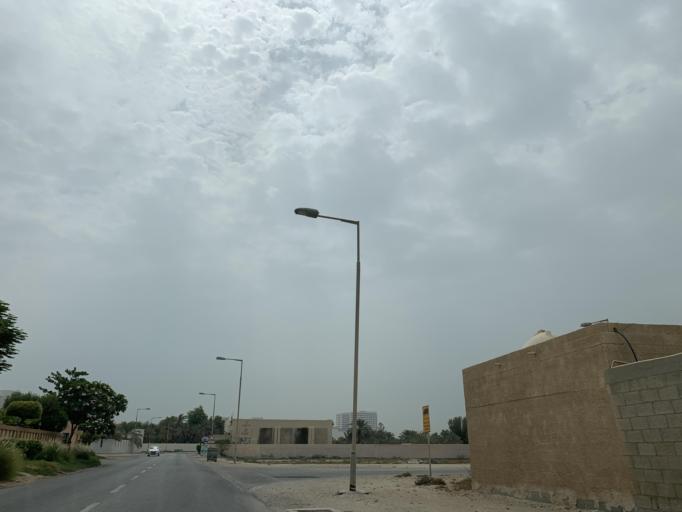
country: BH
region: Central Governorate
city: Madinat Hamad
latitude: 26.1791
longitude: 50.4735
